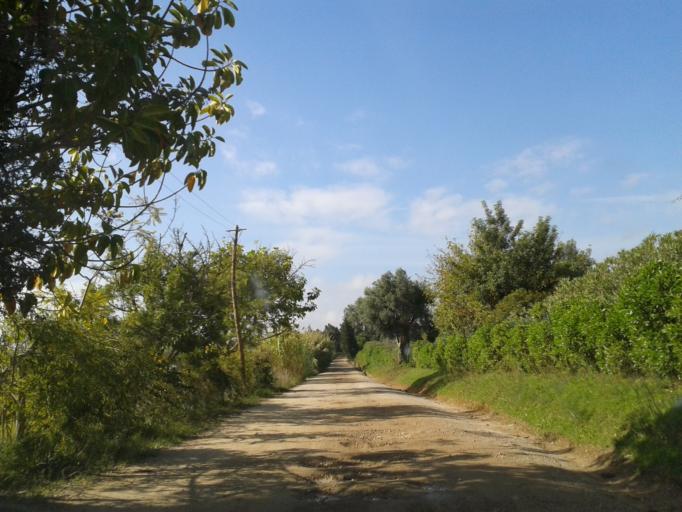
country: PT
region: Faro
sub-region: Tavira
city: Tavira
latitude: 37.1575
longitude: -7.5737
